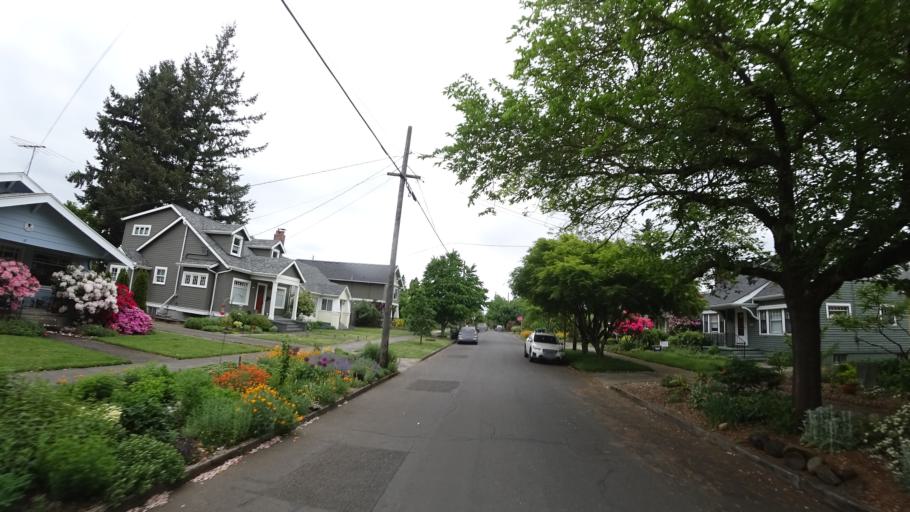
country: US
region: Oregon
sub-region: Multnomah County
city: Portland
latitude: 45.5463
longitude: -122.6087
